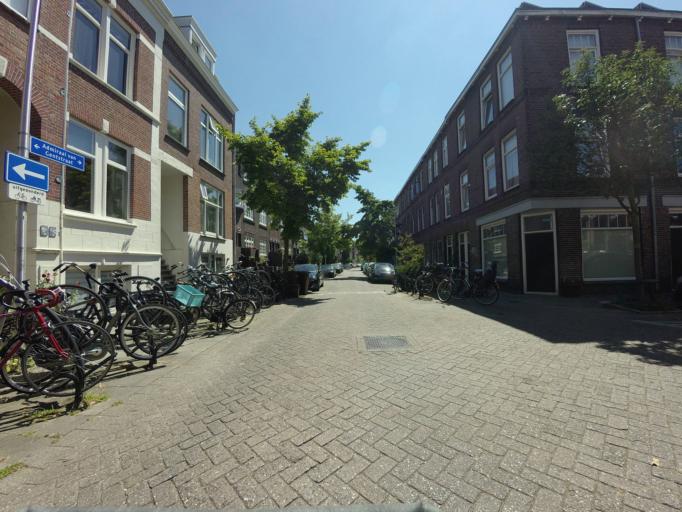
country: NL
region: Utrecht
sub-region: Gemeente Utrecht
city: Utrecht
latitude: 52.1010
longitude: 5.1365
